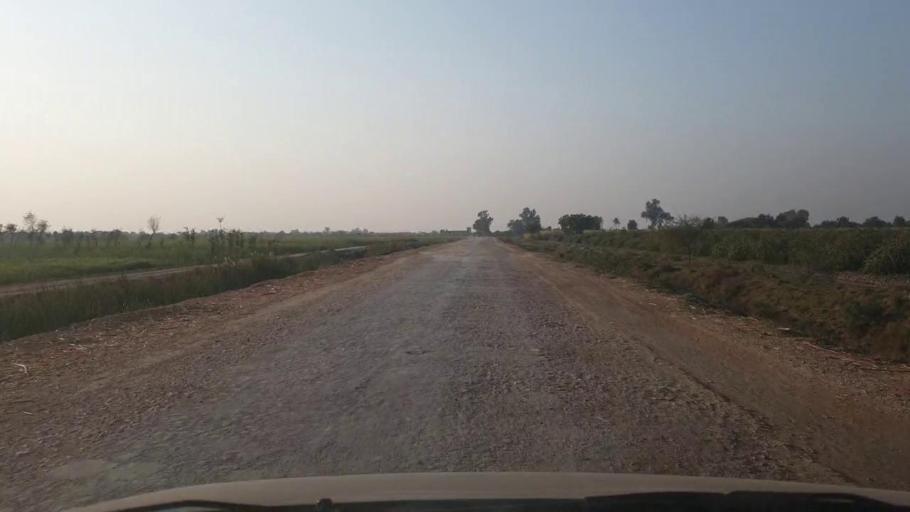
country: PK
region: Sindh
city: Mirwah Gorchani
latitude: 25.3692
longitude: 69.1317
